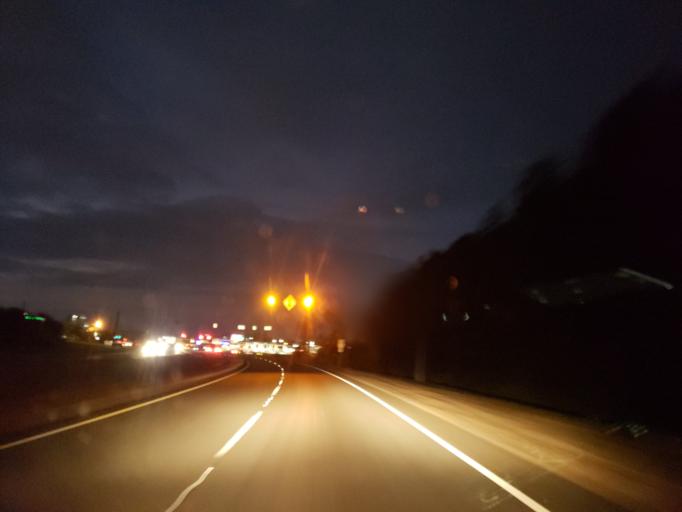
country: US
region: Georgia
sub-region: Polk County
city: Rockmart
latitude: 34.0065
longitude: -85.0268
